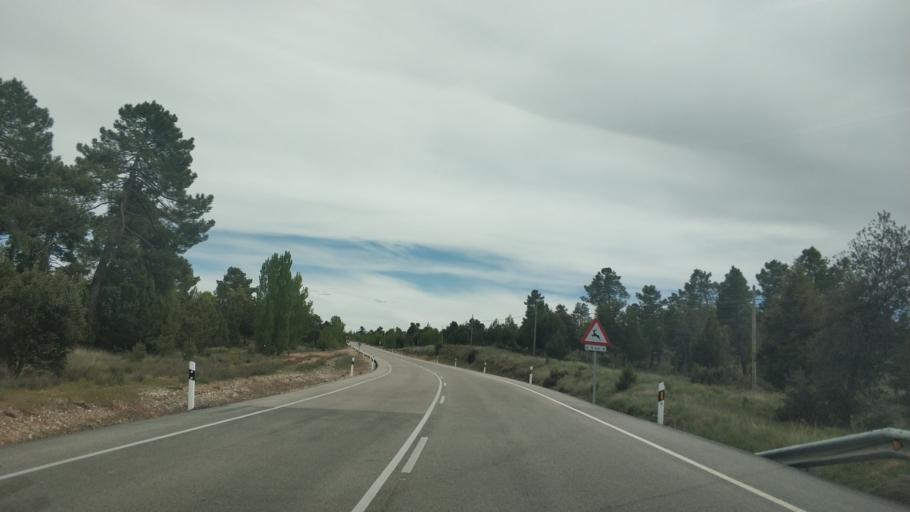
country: ES
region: Castille and Leon
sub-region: Provincia de Soria
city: Valdenebro
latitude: 41.5477
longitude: -2.9609
